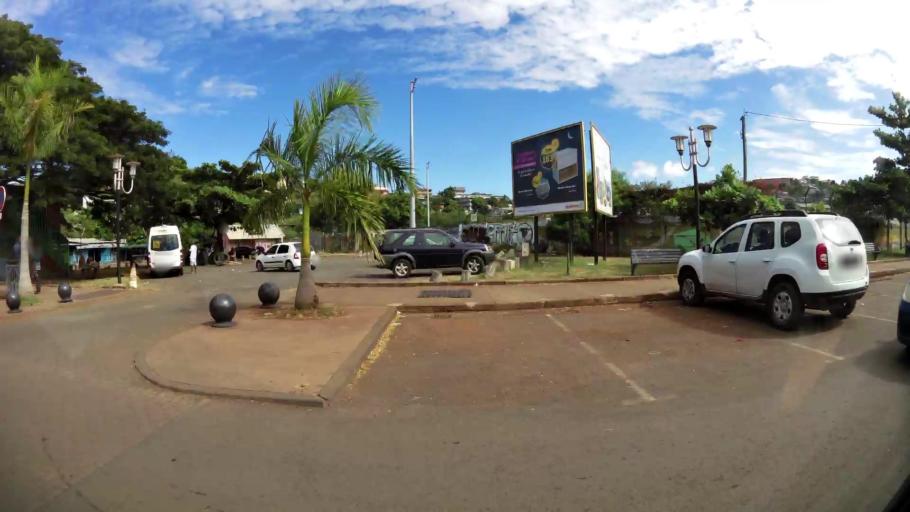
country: YT
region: Mamoudzou
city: Mamoudzou
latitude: -12.7837
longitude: 45.2226
